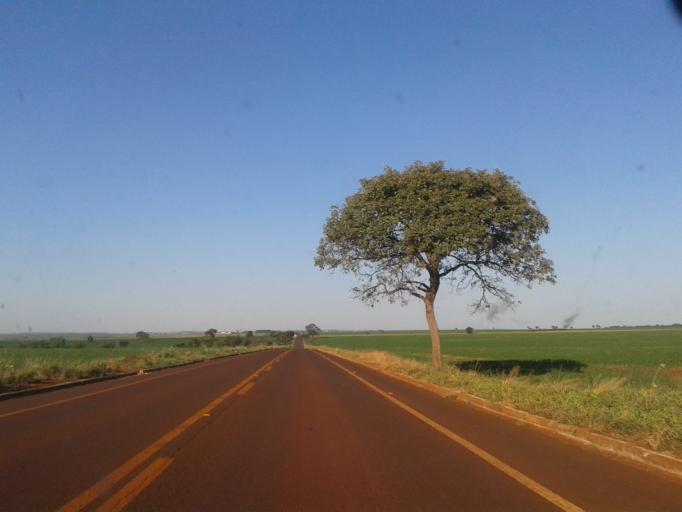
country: BR
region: Minas Gerais
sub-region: Capinopolis
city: Capinopolis
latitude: -18.7111
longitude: -49.7241
